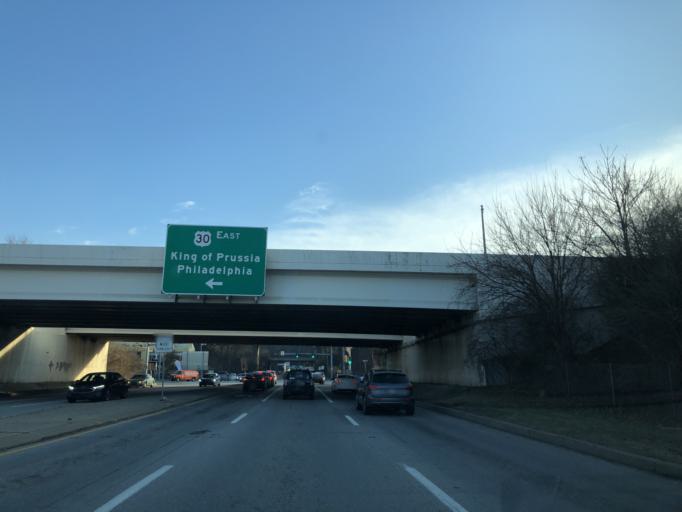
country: US
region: Pennsylvania
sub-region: Chester County
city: Exton
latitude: 40.0213
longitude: -75.6244
